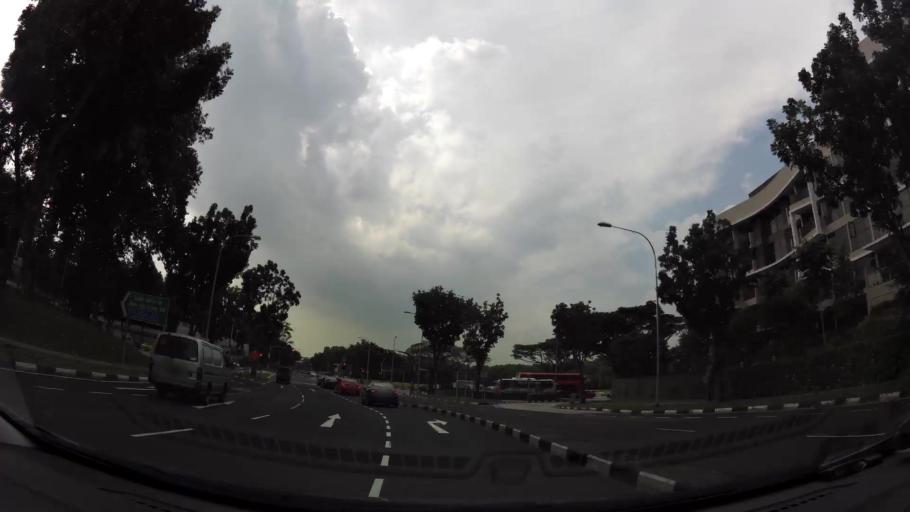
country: SG
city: Singapore
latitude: 1.3383
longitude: 103.9186
